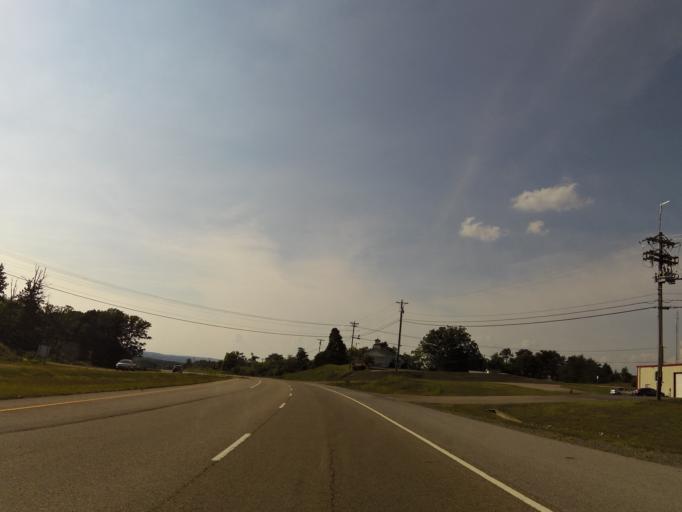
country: US
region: Tennessee
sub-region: Loudon County
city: Lenoir City
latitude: 35.7555
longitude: -84.2171
